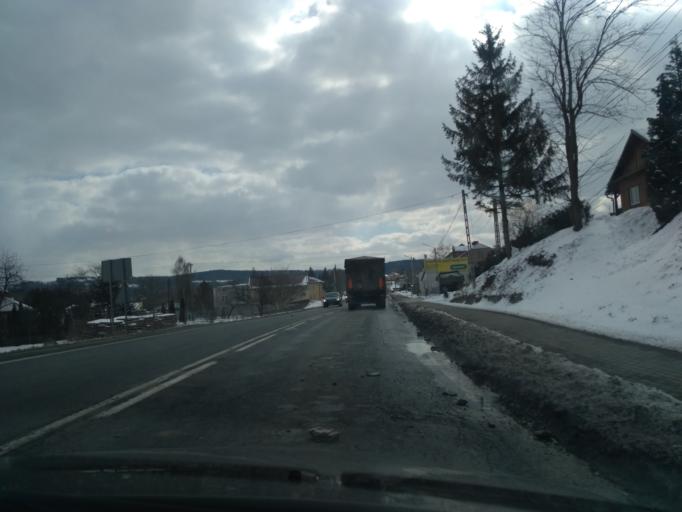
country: PL
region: Subcarpathian Voivodeship
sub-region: Powiat rzeszowski
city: Lutoryz
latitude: 49.9491
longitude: 21.9137
